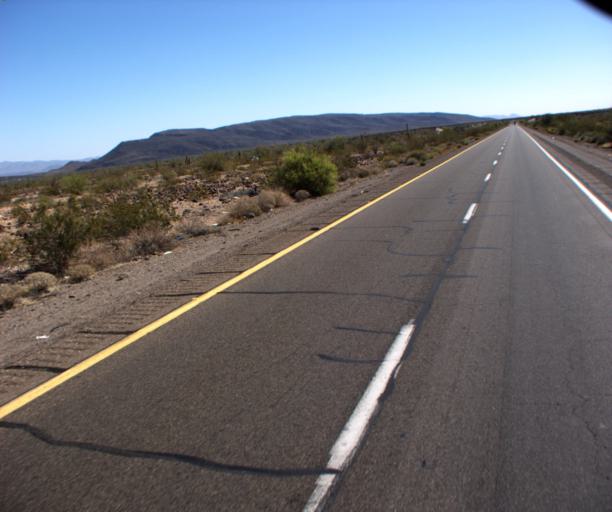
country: US
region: Arizona
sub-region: La Paz County
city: Quartzsite
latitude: 33.6569
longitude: -113.9731
